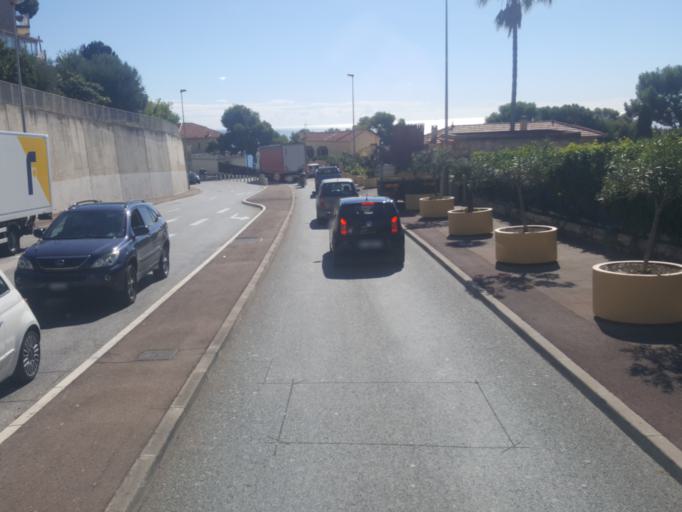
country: FR
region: Provence-Alpes-Cote d'Azur
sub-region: Departement des Alpes-Maritimes
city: Cap-d'Ail
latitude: 43.7250
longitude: 7.4013
